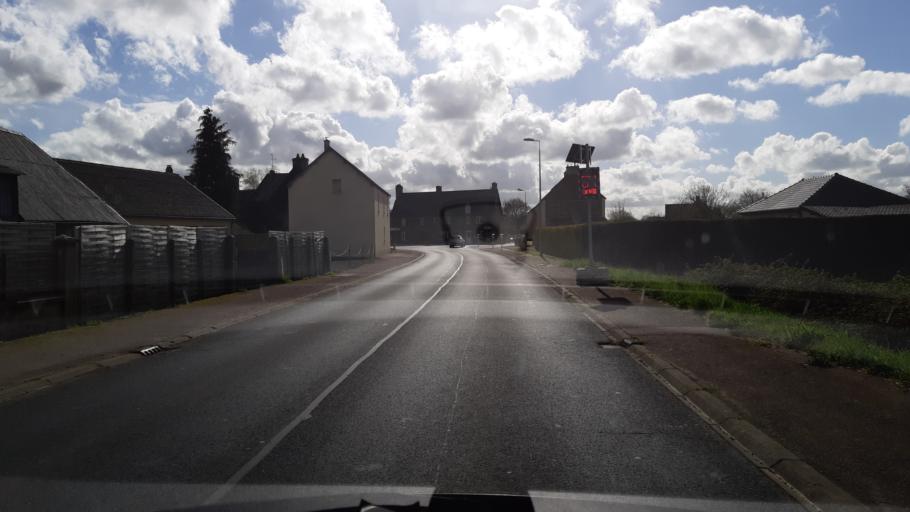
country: FR
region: Lower Normandy
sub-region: Departement de la Manche
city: Agneaux
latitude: 49.0286
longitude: -1.1433
